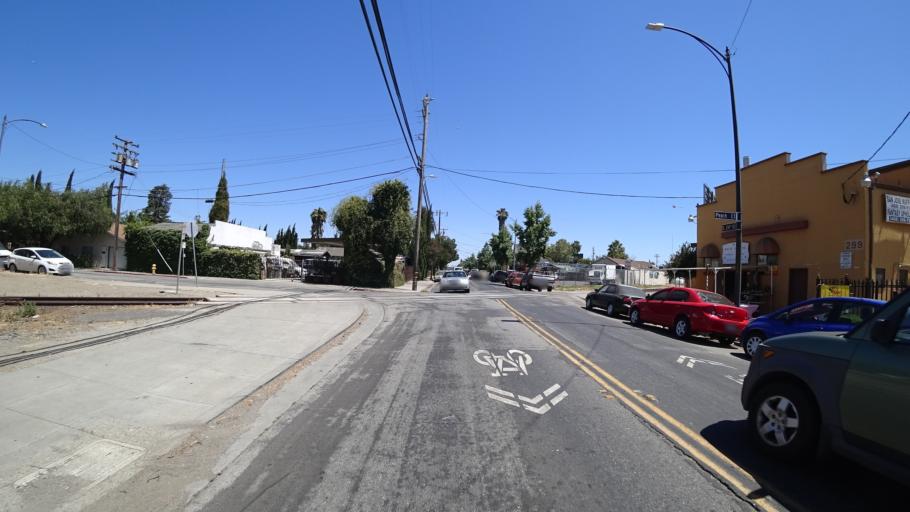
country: US
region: California
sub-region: Santa Clara County
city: San Jose
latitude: 37.3424
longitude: -121.8633
